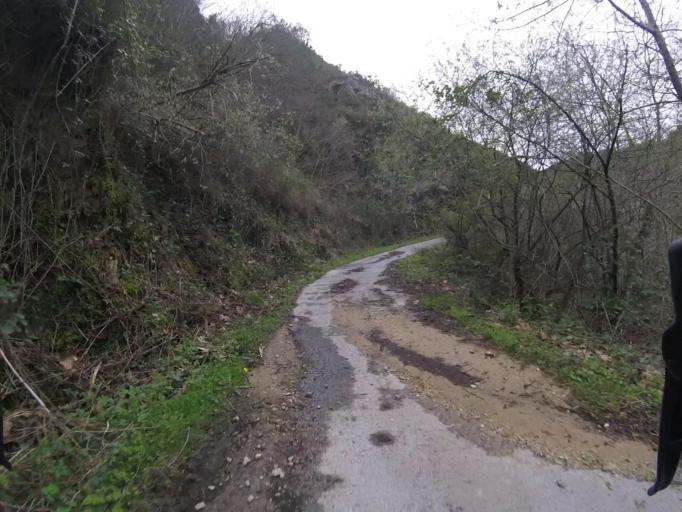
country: ES
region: Navarre
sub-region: Provincia de Navarra
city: Bera
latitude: 43.2939
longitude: -1.7316
